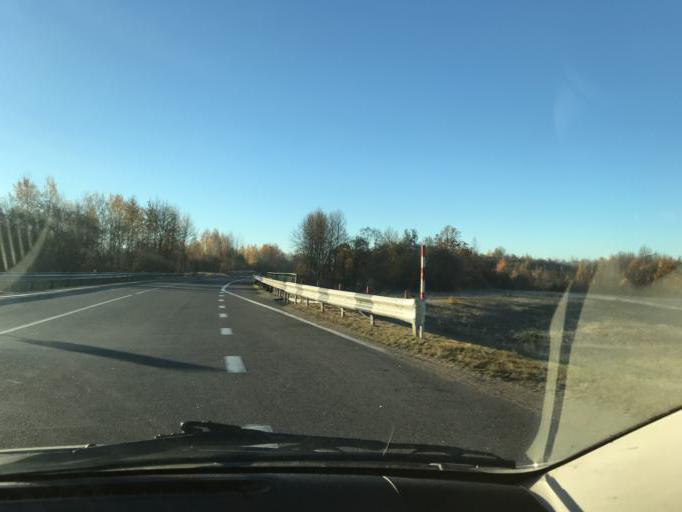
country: BY
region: Vitebsk
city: Vitebsk
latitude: 55.0876
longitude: 30.3084
